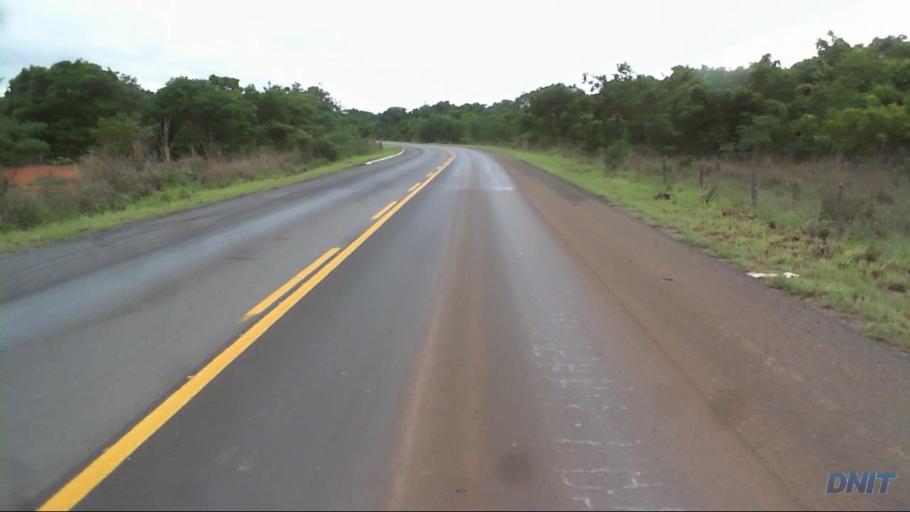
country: BR
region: Goias
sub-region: Padre Bernardo
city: Padre Bernardo
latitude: -15.2196
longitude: -48.5506
